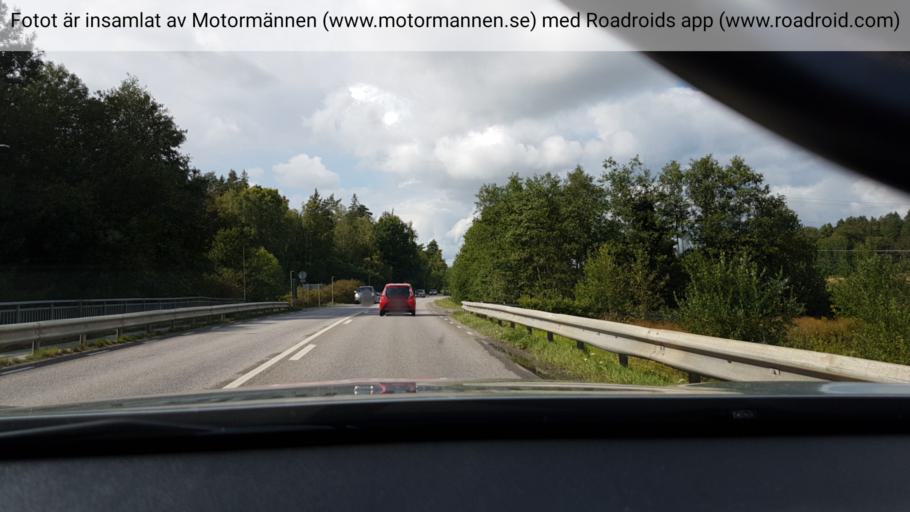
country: SE
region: Stockholm
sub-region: Ekero Kommun
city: Ekeroe
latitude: 59.3050
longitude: 17.7804
